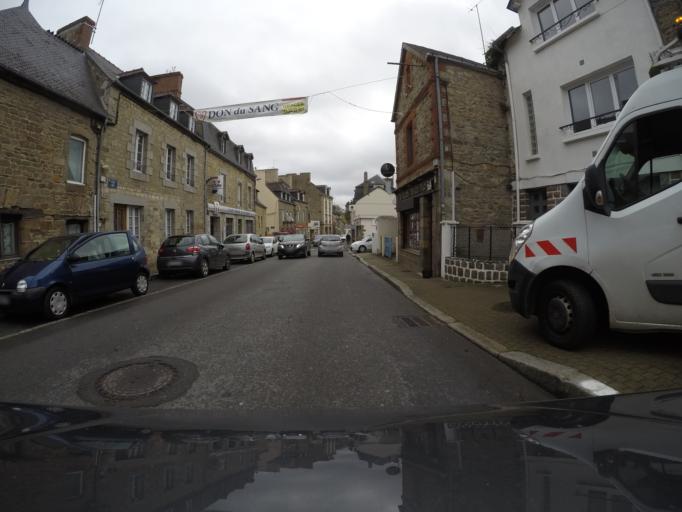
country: FR
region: Brittany
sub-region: Departement des Cotes-d'Armor
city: Guingamp
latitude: 48.5610
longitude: -3.1579
